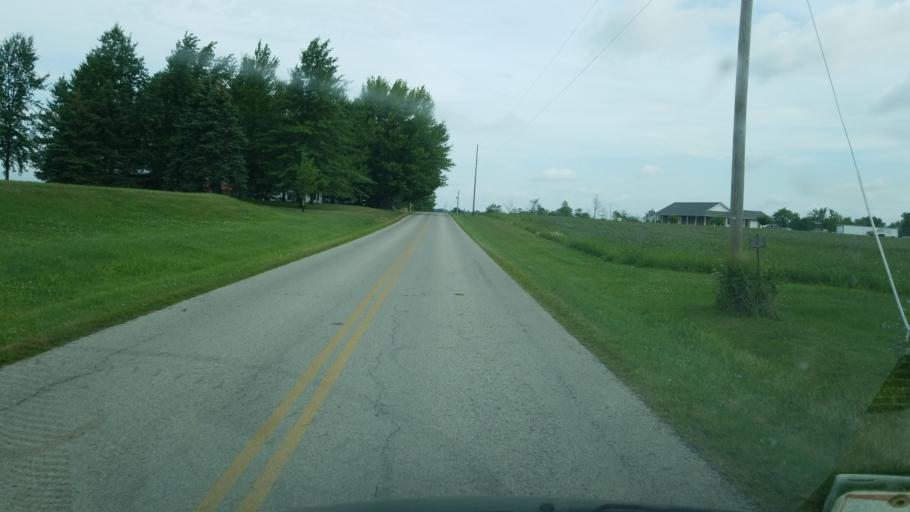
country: US
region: Ohio
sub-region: Seneca County
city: Tiffin
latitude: 41.1026
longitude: -83.0930
